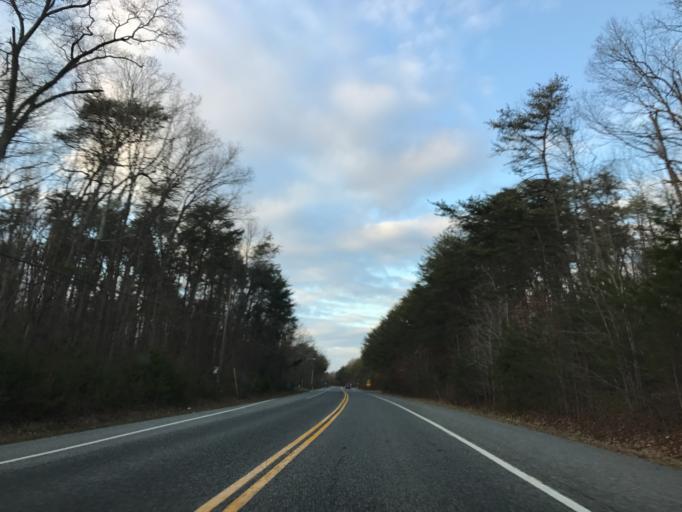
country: US
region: Maryland
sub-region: Cecil County
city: Charlestown
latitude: 39.5456
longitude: -75.9481
